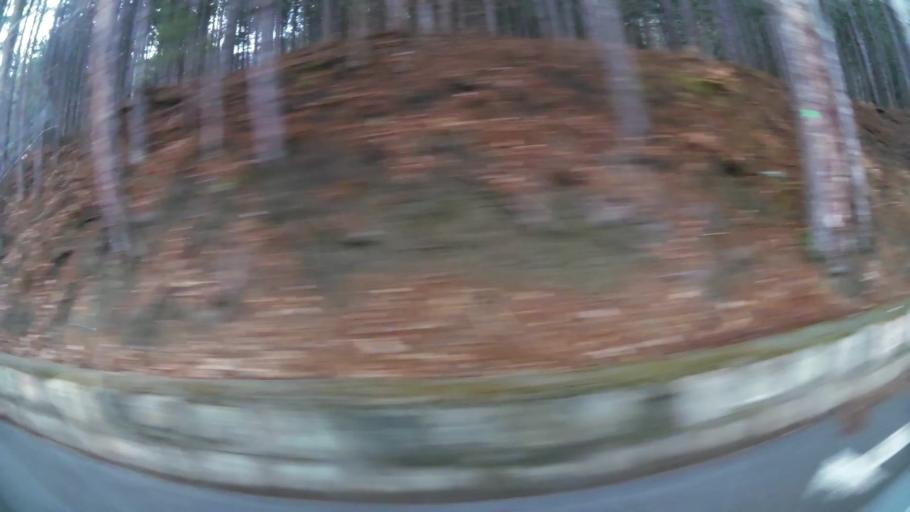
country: BG
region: Sofia-Capital
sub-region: Stolichna Obshtina
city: Sofia
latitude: 42.5846
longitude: 23.4284
